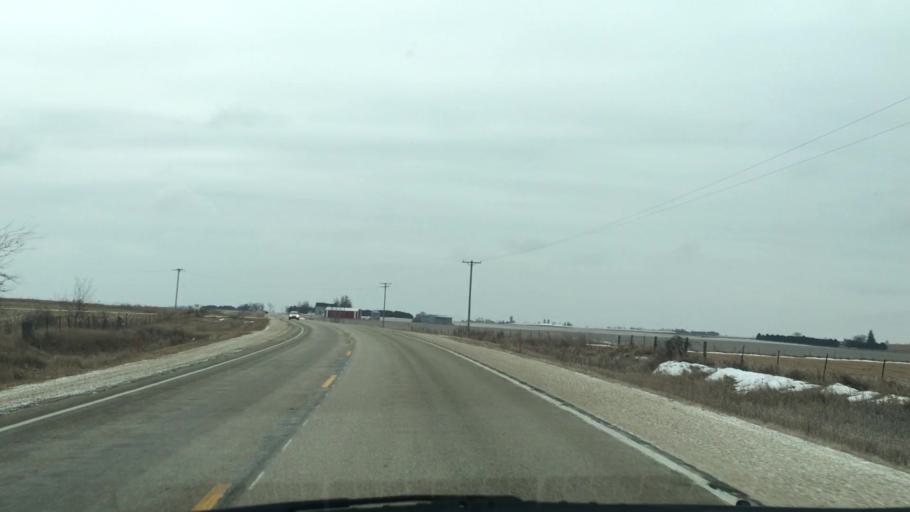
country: US
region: Iowa
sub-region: Fayette County
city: West Union
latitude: 43.0328
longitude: -91.8362
